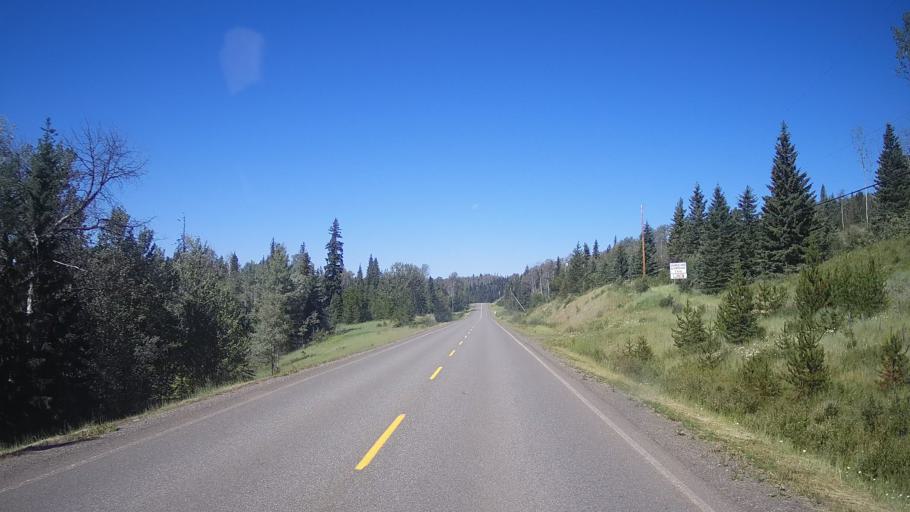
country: CA
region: British Columbia
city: Kamloops
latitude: 51.5046
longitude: -120.6132
